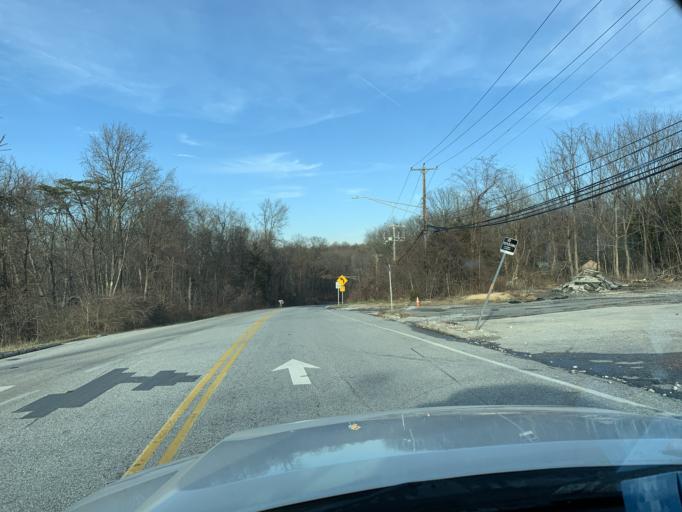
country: US
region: Maryland
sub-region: Anne Arundel County
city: Jessup
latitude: 39.1421
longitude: -76.7588
